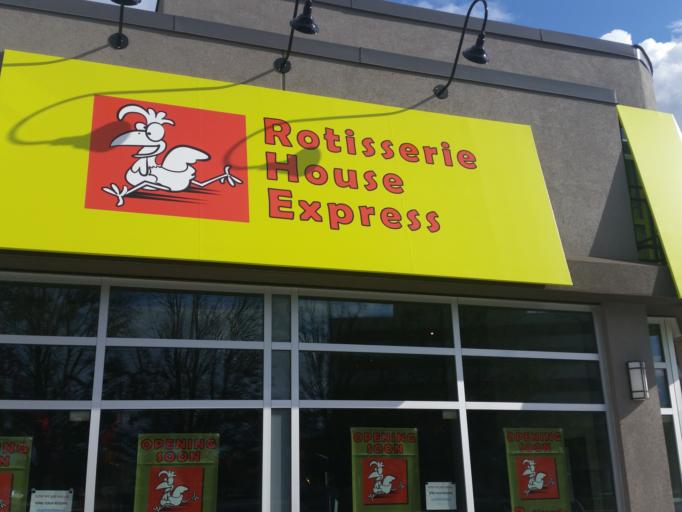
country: CA
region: Ontario
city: Bells Corners
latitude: 45.3477
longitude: -75.7870
